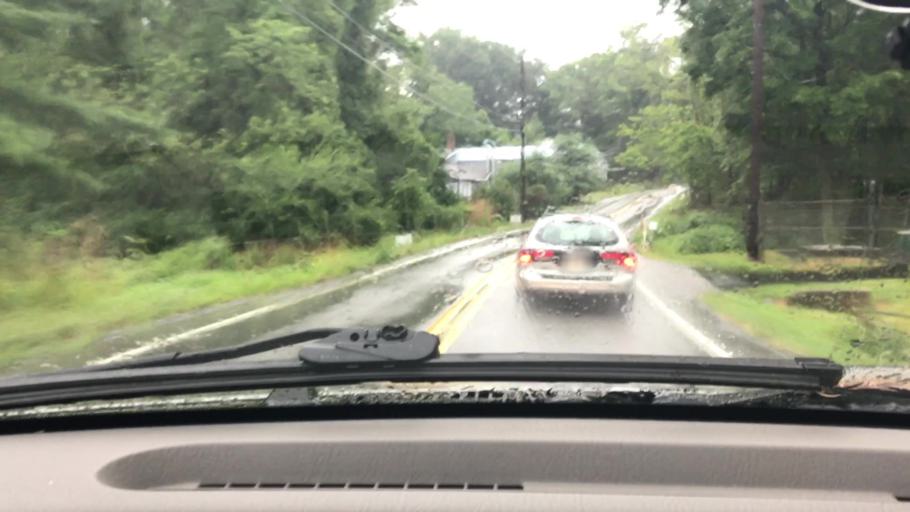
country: US
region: Pennsylvania
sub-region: Lancaster County
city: Elizabethtown
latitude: 40.1472
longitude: -76.6247
